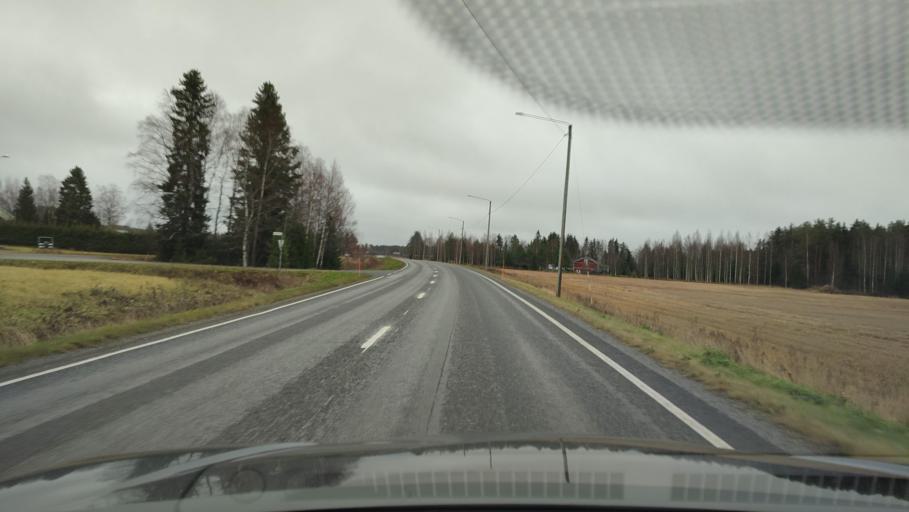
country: FI
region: Southern Ostrobothnia
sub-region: Suupohja
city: Isojoki
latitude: 62.1821
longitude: 21.8143
